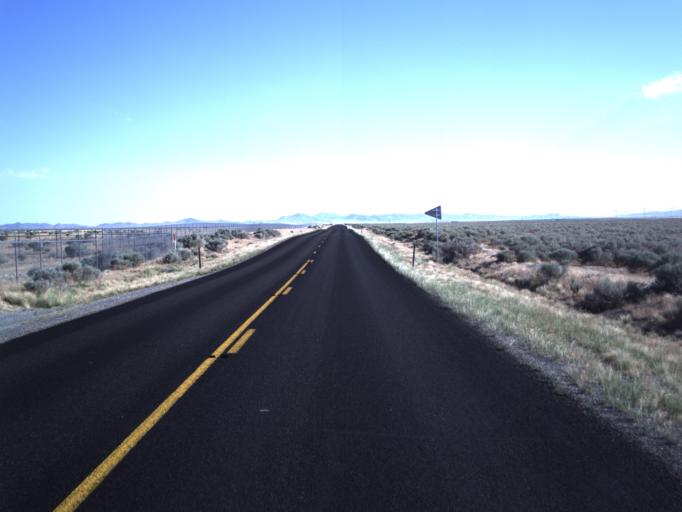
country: US
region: Utah
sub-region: Beaver County
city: Milford
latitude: 38.4211
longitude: -113.0099
